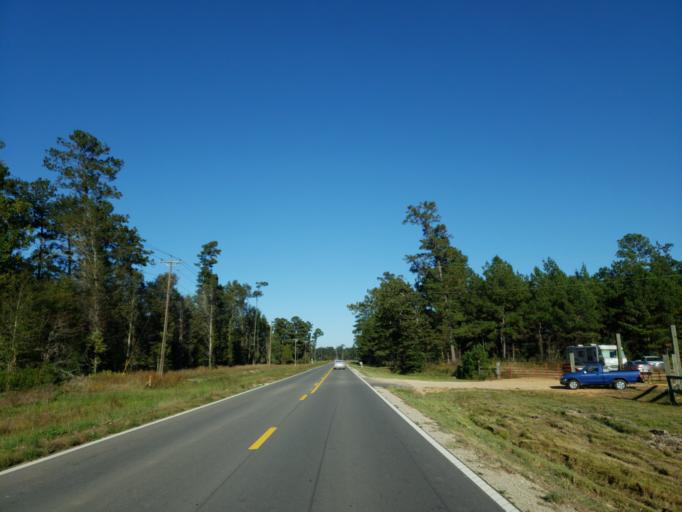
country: US
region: Mississippi
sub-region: Forrest County
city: Petal
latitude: 31.3681
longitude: -89.1345
